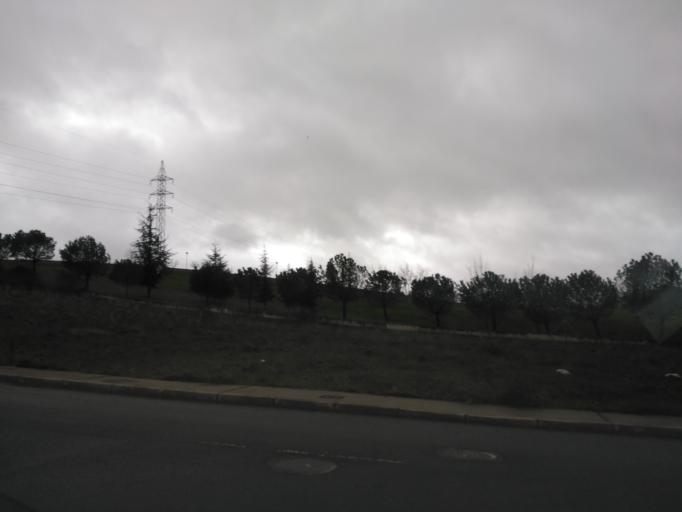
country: ES
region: Castille and Leon
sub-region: Provincia de Salamanca
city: Villamayor
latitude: 40.9806
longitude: -5.6979
